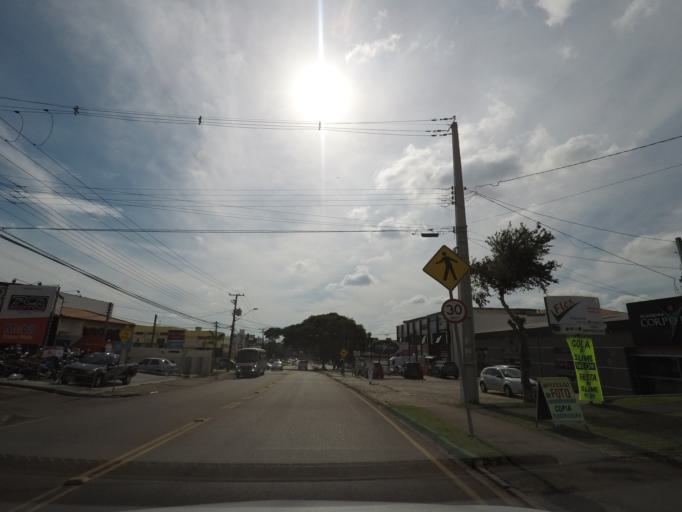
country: BR
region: Parana
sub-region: Curitiba
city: Curitiba
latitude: -25.4680
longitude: -49.2403
